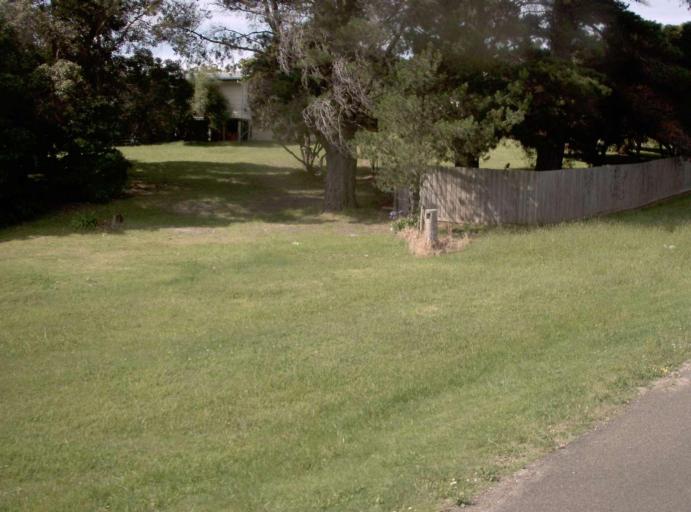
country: AU
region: Victoria
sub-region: East Gippsland
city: Lakes Entrance
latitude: -37.8656
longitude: 148.0206
